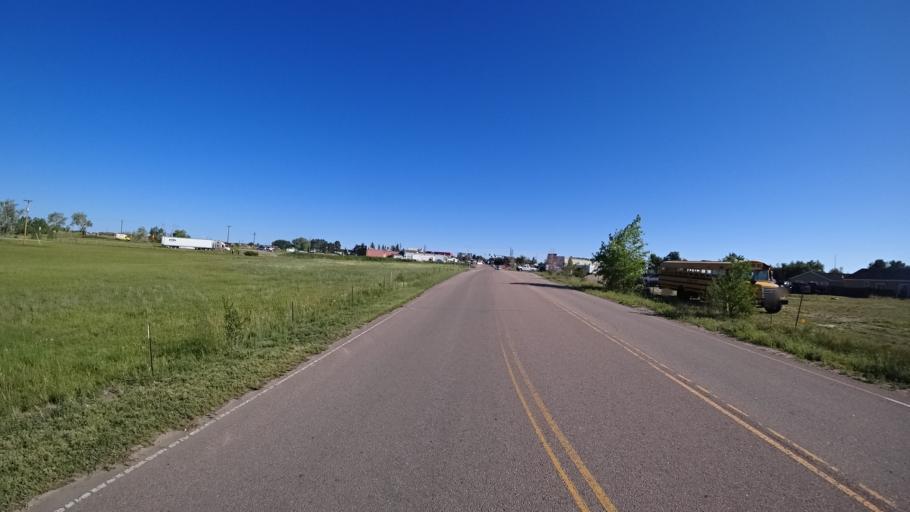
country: US
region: Colorado
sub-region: El Paso County
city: Cimarron Hills
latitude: 38.9312
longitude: -104.6084
